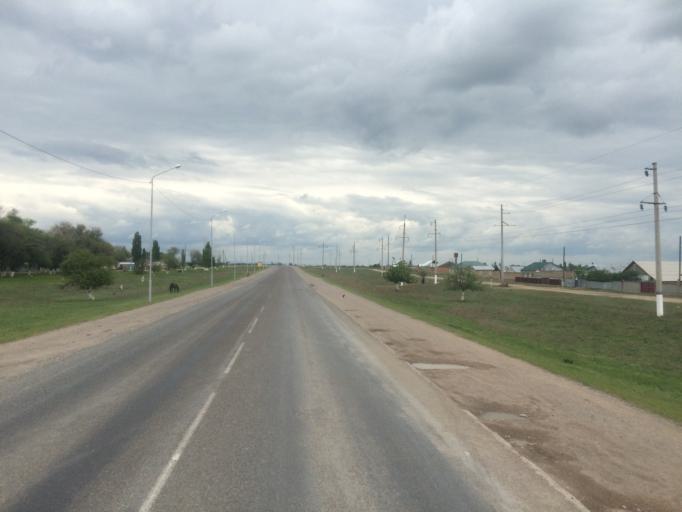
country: KG
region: Chuy
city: Sokuluk
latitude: 43.2480
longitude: 74.2954
